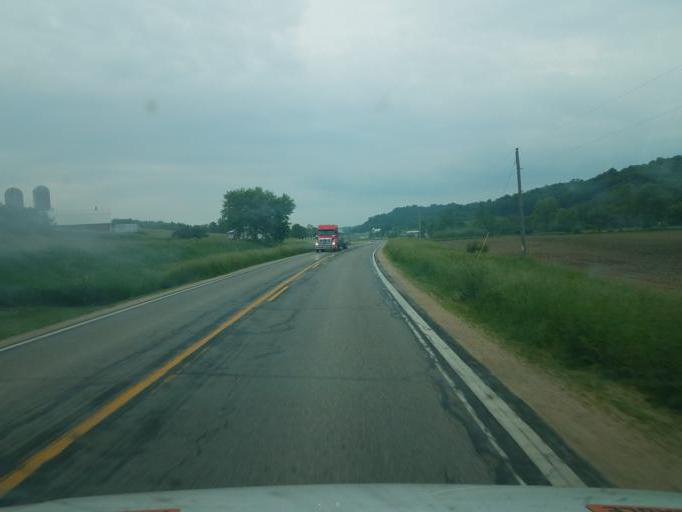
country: US
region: Wisconsin
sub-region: Vernon County
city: Hillsboro
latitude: 43.6550
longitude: -90.3921
